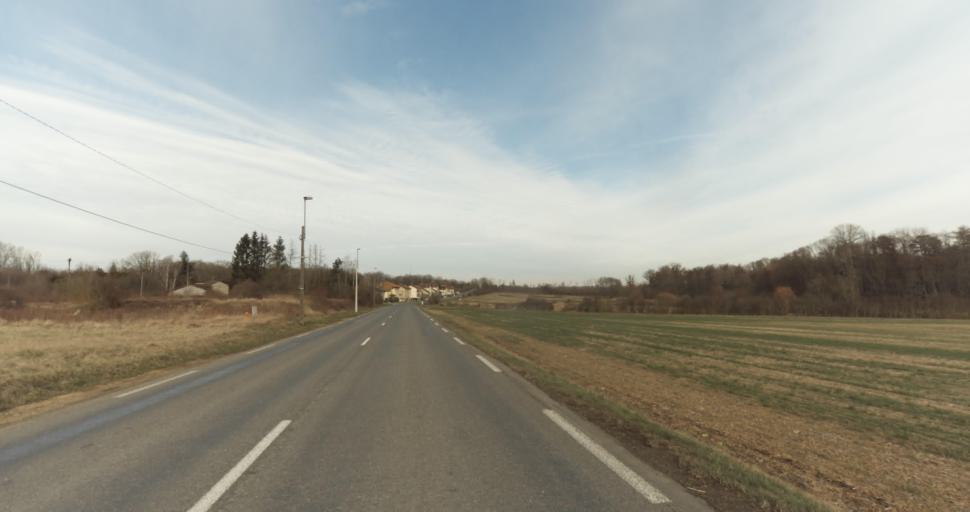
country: FR
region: Lorraine
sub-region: Departement de Meurthe-et-Moselle
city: Jarny
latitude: 49.1426
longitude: 5.8882
